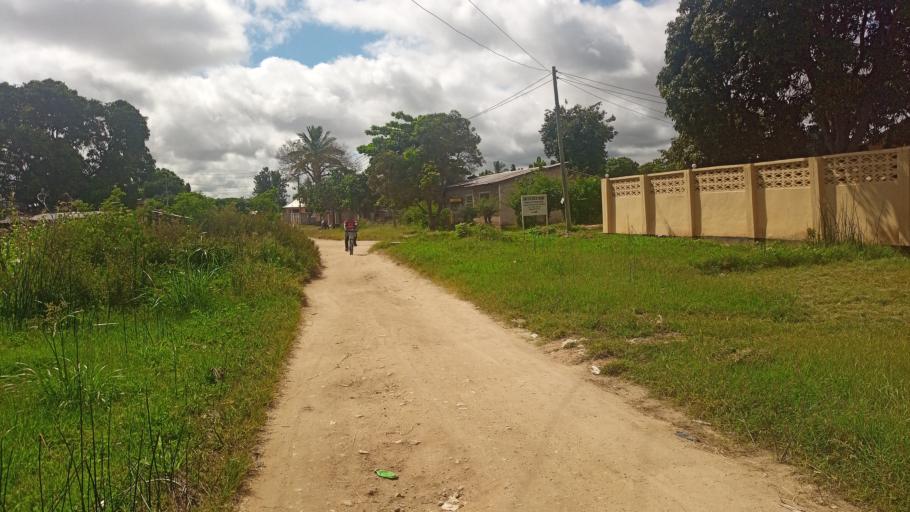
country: TZ
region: Dodoma
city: Dodoma
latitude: -6.1907
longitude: 35.7321
